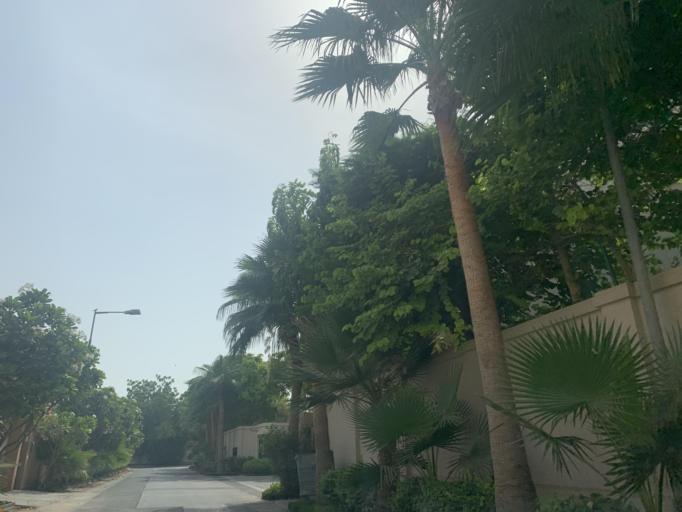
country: BH
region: Manama
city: Jidd Hafs
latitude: 26.1987
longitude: 50.4806
